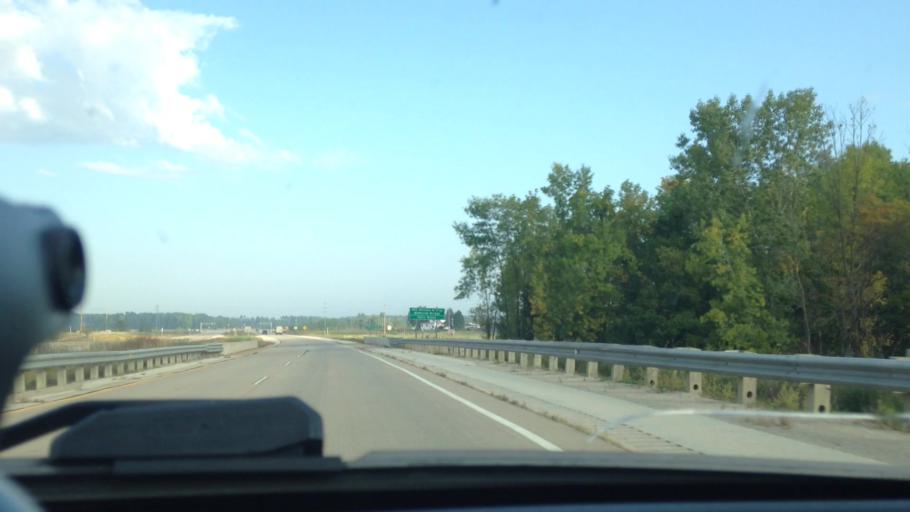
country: US
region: Wisconsin
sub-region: Oconto County
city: Oconto Falls
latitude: 44.9768
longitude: -88.0406
